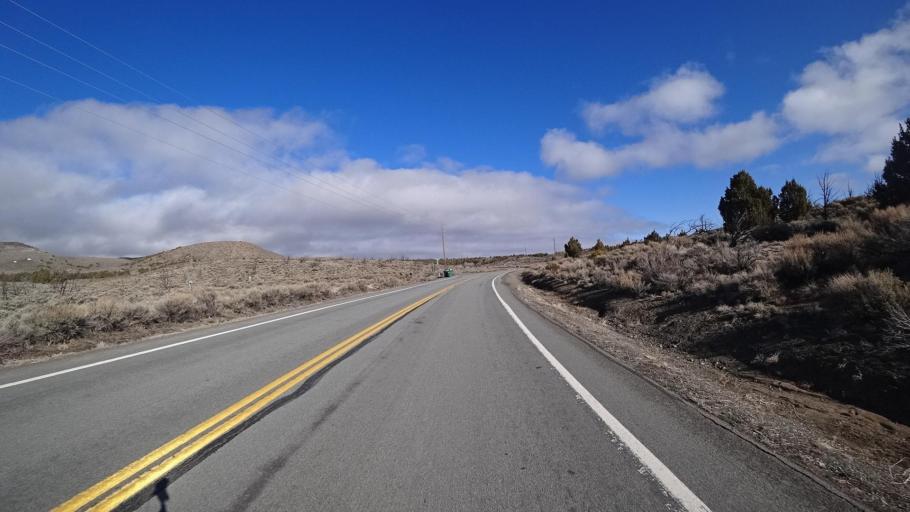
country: US
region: Nevada
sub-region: Washoe County
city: Cold Springs
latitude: 39.7733
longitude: -119.8924
